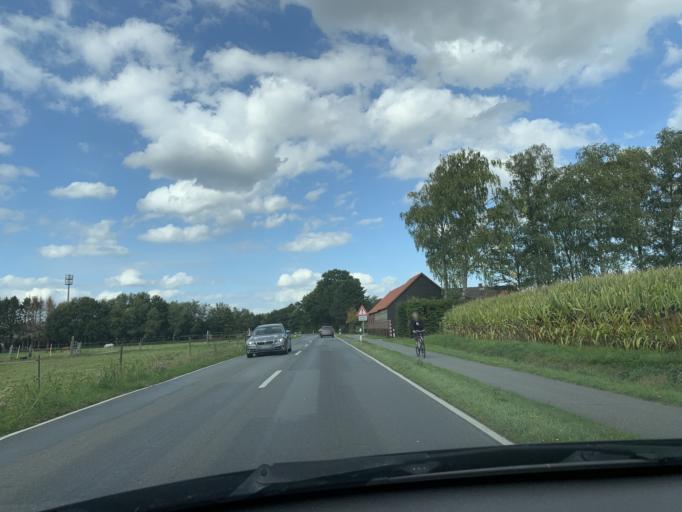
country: DE
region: Lower Saxony
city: Edewecht
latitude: 53.1485
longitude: 7.9988
